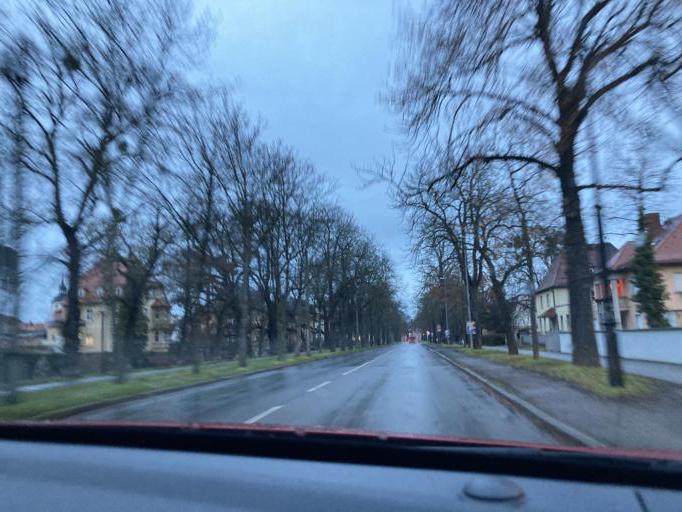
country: DE
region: Saxony-Anhalt
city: Naumburg
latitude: 51.1525
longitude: 11.8144
